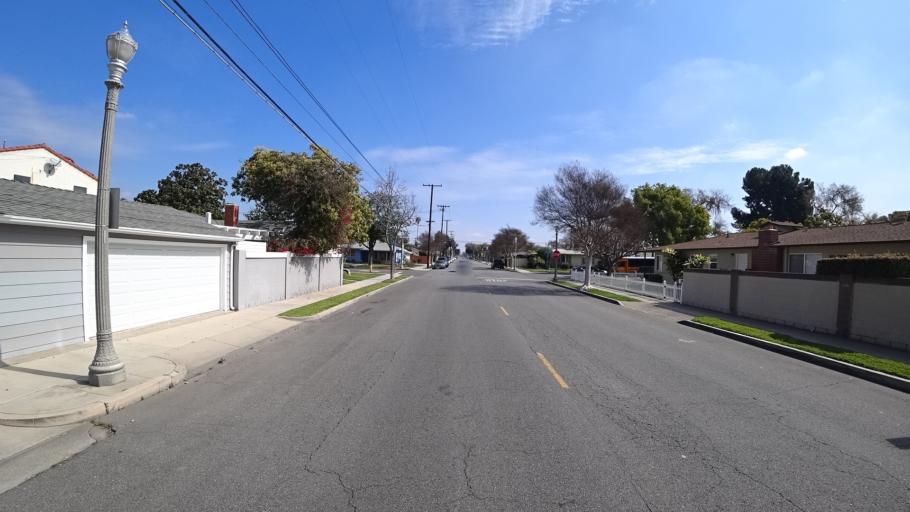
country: US
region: California
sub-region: Orange County
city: Anaheim
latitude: 33.8267
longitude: -117.9216
